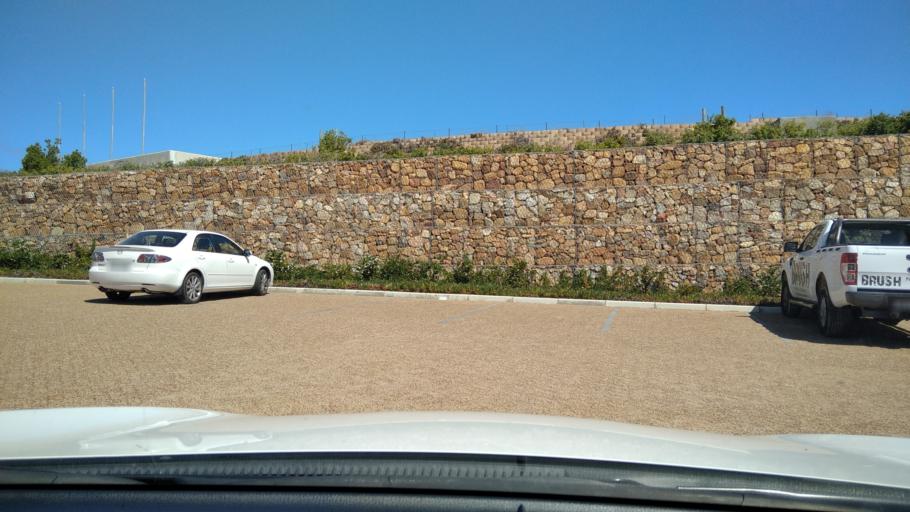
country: ZA
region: Western Cape
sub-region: Overberg District Municipality
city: Hermanus
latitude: -34.3462
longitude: 19.1352
